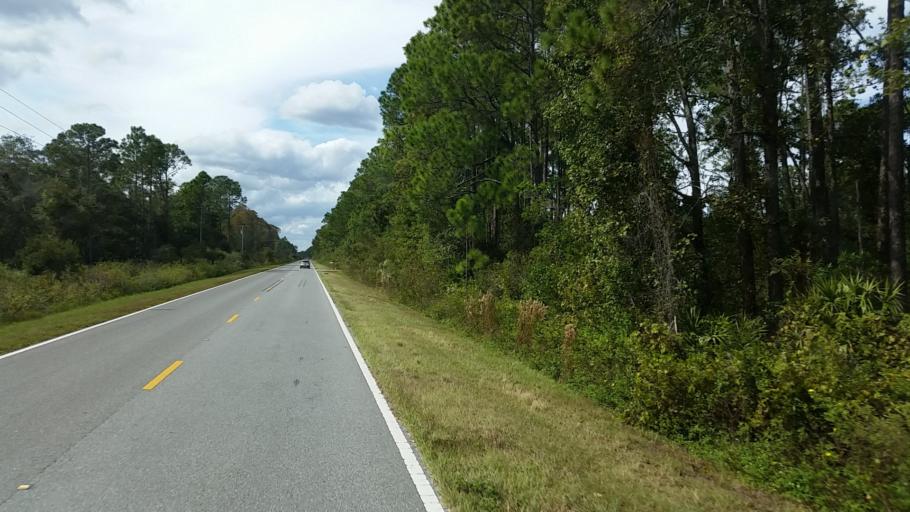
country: US
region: Florida
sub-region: Lake County
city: Four Corners
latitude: 28.3761
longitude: -81.7761
